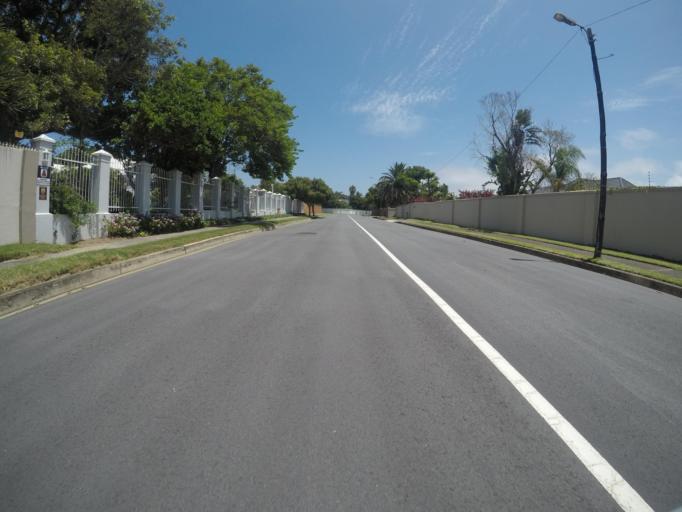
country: ZA
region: Eastern Cape
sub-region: Buffalo City Metropolitan Municipality
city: East London
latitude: -32.9963
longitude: 27.9289
